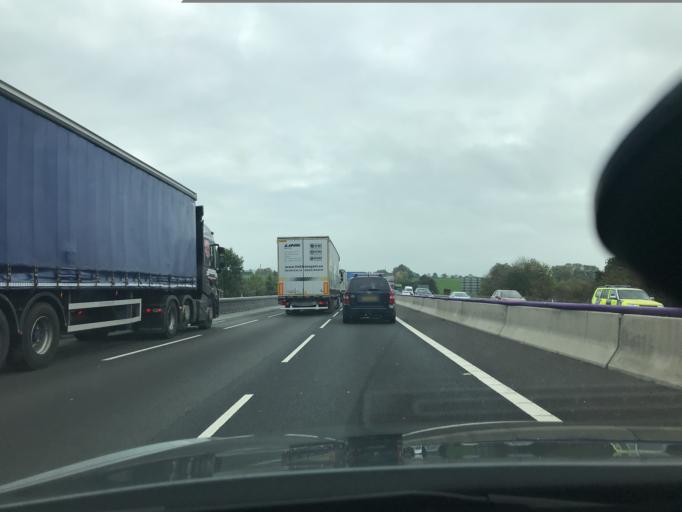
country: GB
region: England
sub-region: Cheshire East
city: Holmes Chapel
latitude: 53.2093
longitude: -2.3879
